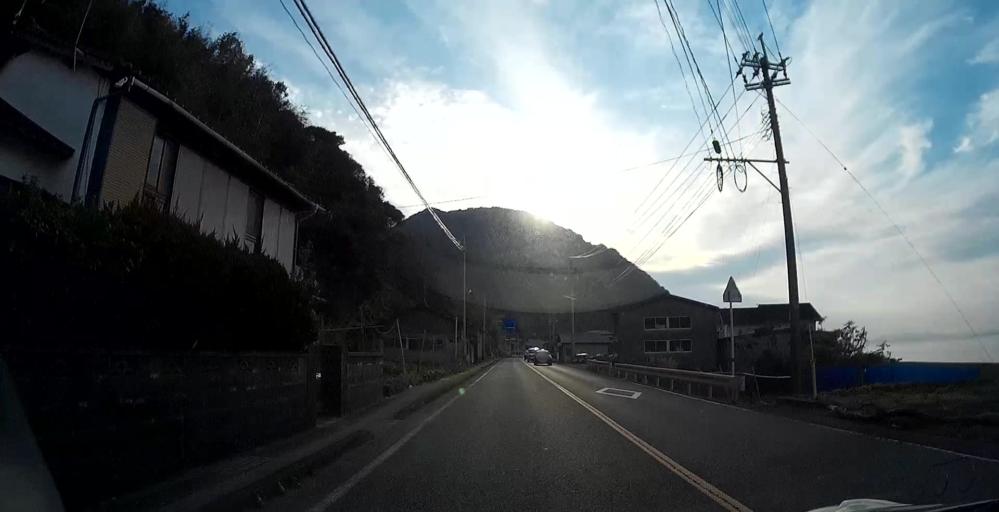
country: JP
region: Nagasaki
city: Shimabara
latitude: 32.6388
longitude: 130.4774
